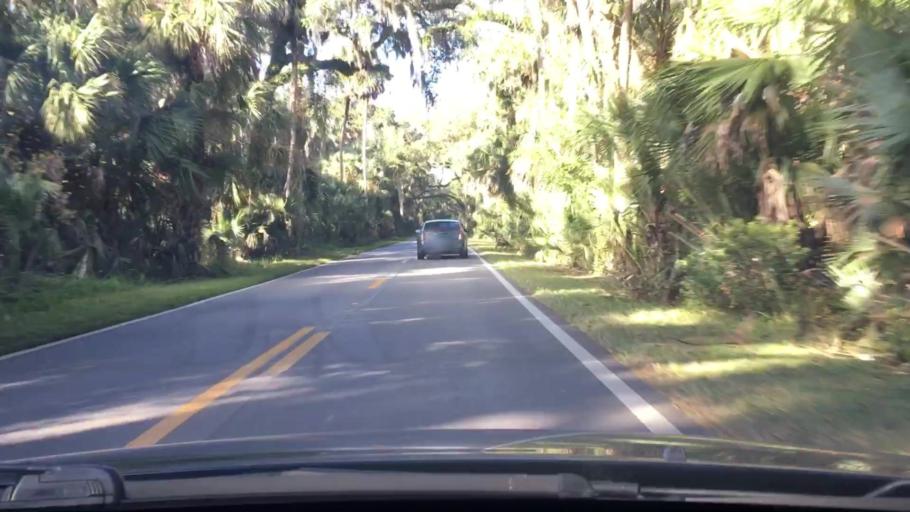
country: US
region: Florida
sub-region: Volusia County
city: Ormond-by-the-Sea
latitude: 29.3913
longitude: -81.1335
